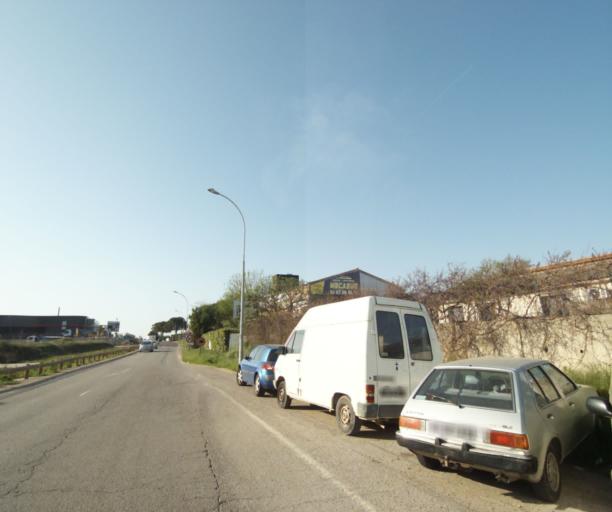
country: FR
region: Languedoc-Roussillon
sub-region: Departement de l'Herault
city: Laverune
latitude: 43.5909
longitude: 3.8004
